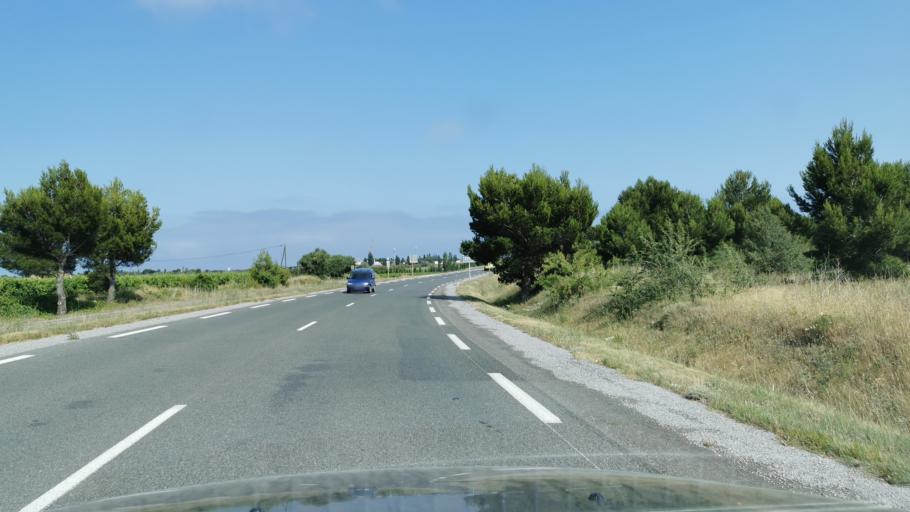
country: FR
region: Languedoc-Roussillon
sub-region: Departement de l'Aude
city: Gruissan
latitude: 43.1211
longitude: 3.0998
